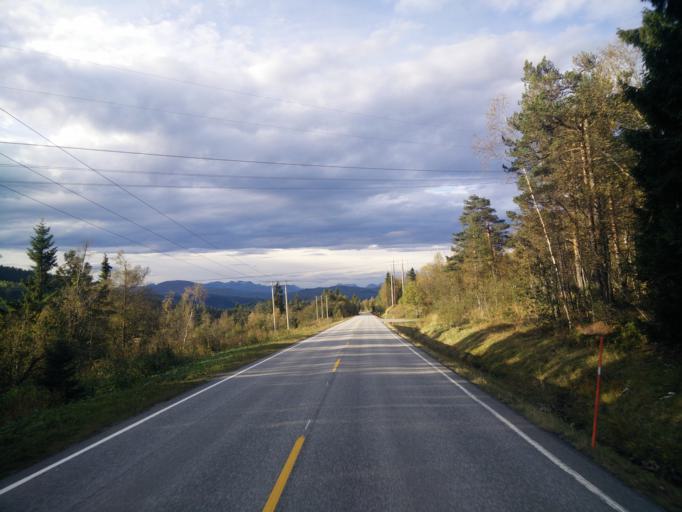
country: NO
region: More og Romsdal
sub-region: Molde
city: Hjelset
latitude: 62.8118
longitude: 7.5903
